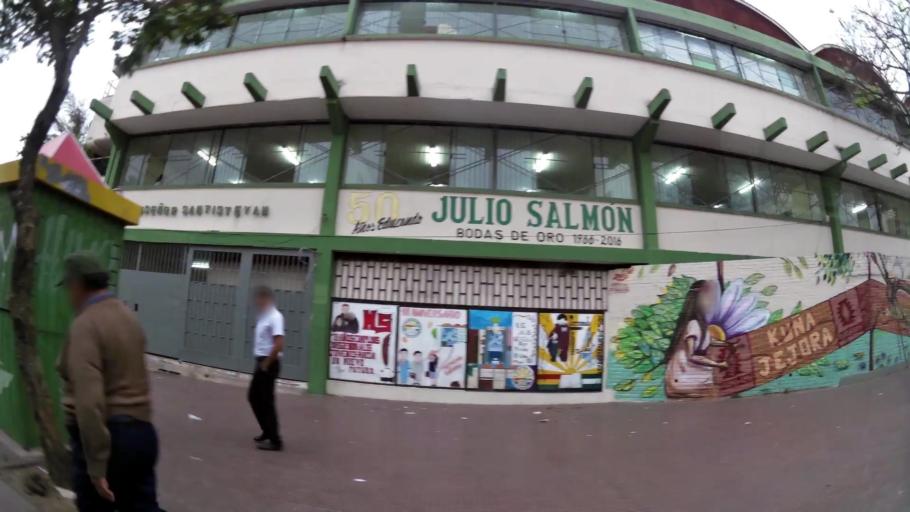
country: BO
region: Santa Cruz
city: Santa Cruz de la Sierra
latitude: -17.7795
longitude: -63.1812
